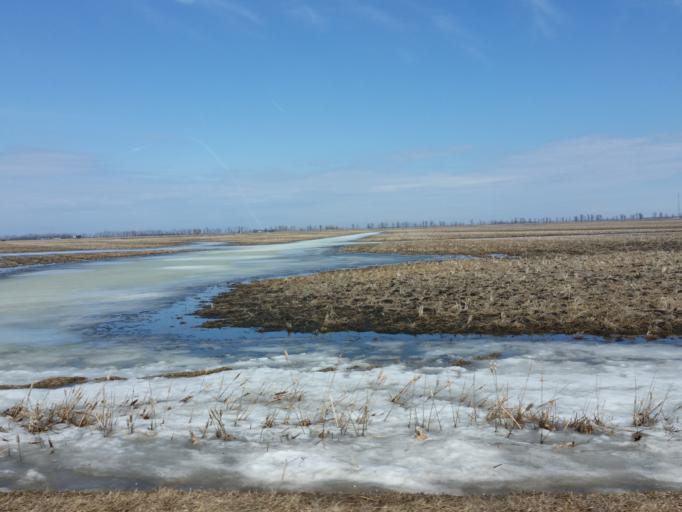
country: US
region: North Dakota
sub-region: Walsh County
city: Grafton
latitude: 48.3243
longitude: -97.1835
